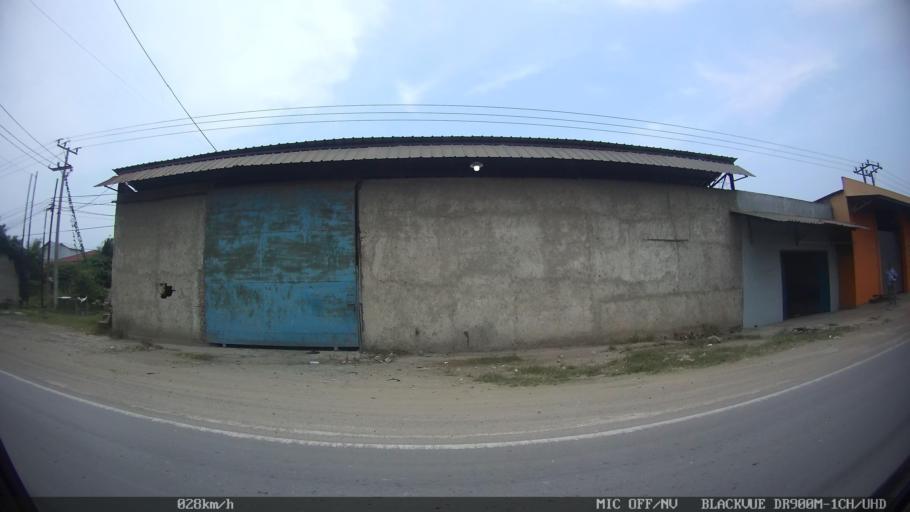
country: ID
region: Lampung
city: Panjang
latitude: -5.4308
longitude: 105.3262
